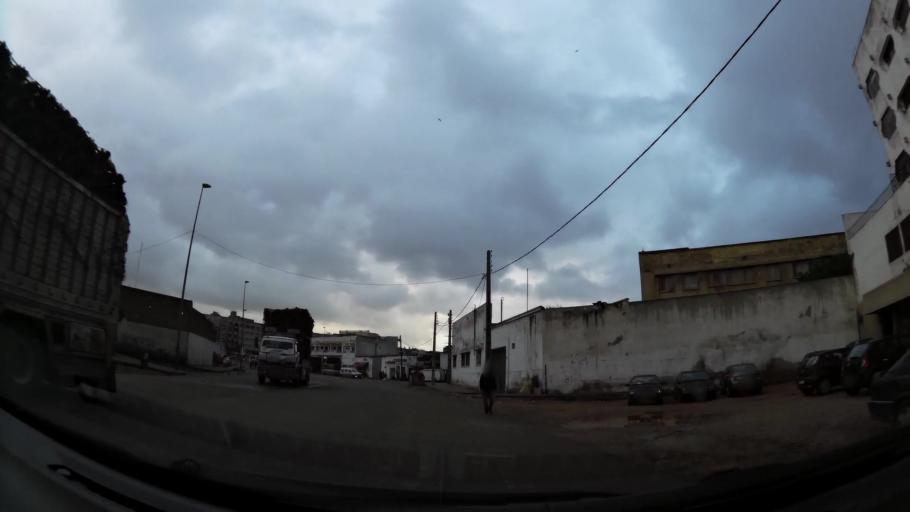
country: MA
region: Grand Casablanca
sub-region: Casablanca
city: Casablanca
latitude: 33.5640
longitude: -7.5969
